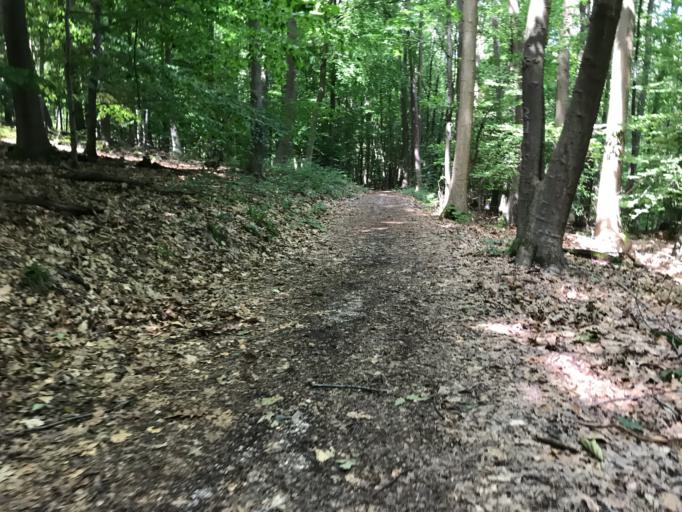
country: DE
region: Rheinland-Pfalz
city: Weiler
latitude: 49.9703
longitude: 7.8703
